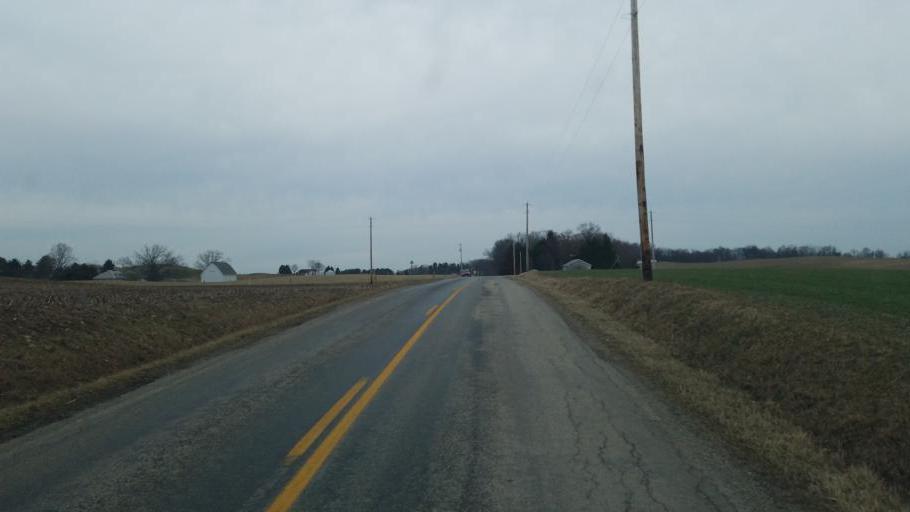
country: US
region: Ohio
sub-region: Ashland County
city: Loudonville
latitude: 40.6156
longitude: -82.2254
